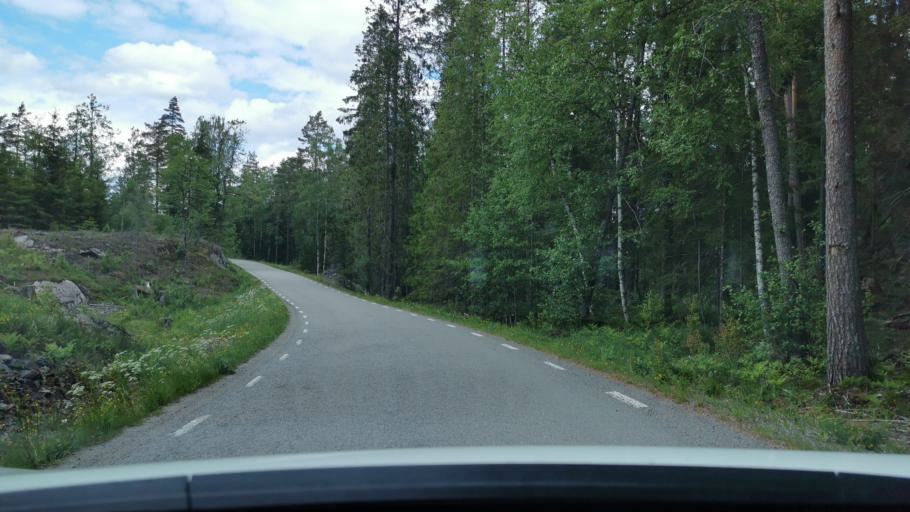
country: SE
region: Vaestra Goetaland
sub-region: Bengtsfors Kommun
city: Dals Langed
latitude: 58.8552
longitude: 12.3303
